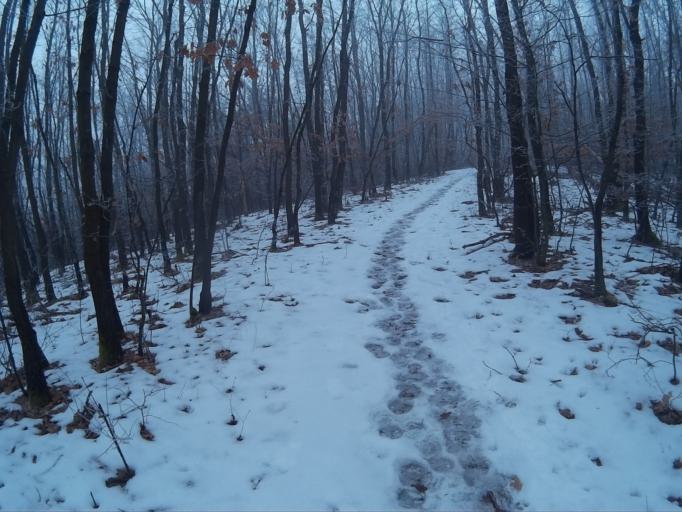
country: HU
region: Nograd
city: Matraverebely
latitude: 47.9651
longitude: 19.7944
